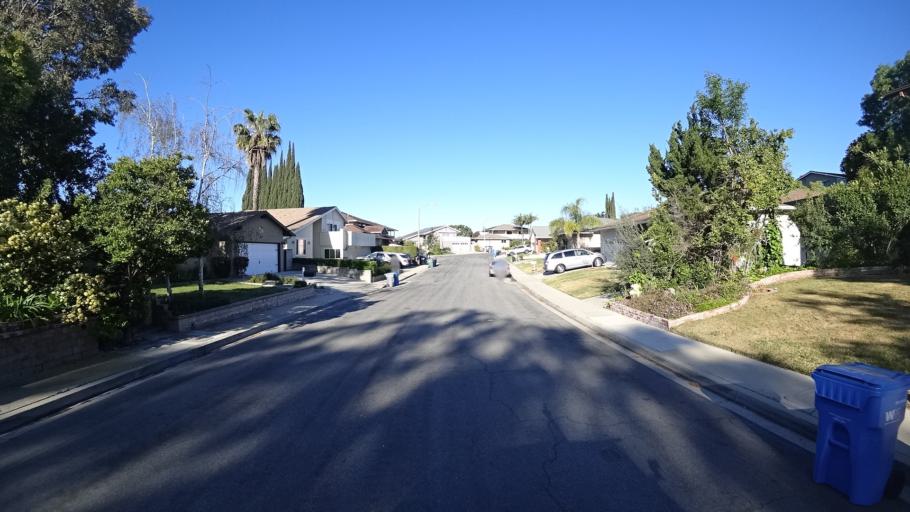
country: US
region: California
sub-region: Ventura County
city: Casa Conejo
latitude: 34.2147
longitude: -118.8953
